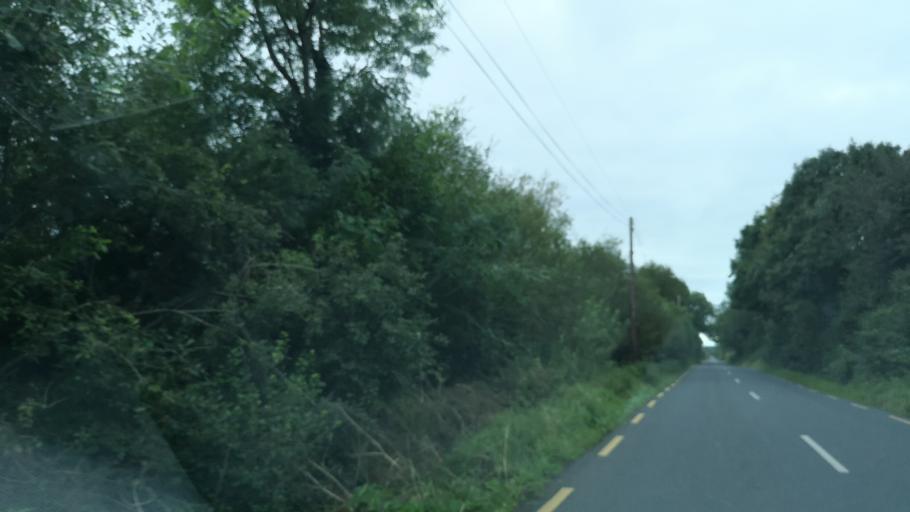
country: IE
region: Leinster
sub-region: Uibh Fhaili
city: Ferbane
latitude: 53.2304
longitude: -7.7754
